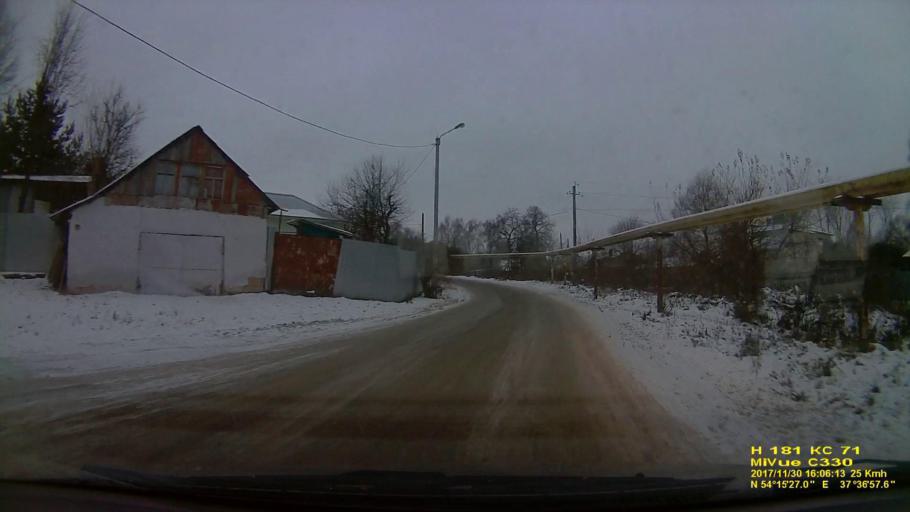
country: RU
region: Tula
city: Gorelki
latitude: 54.2575
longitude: 37.6159
